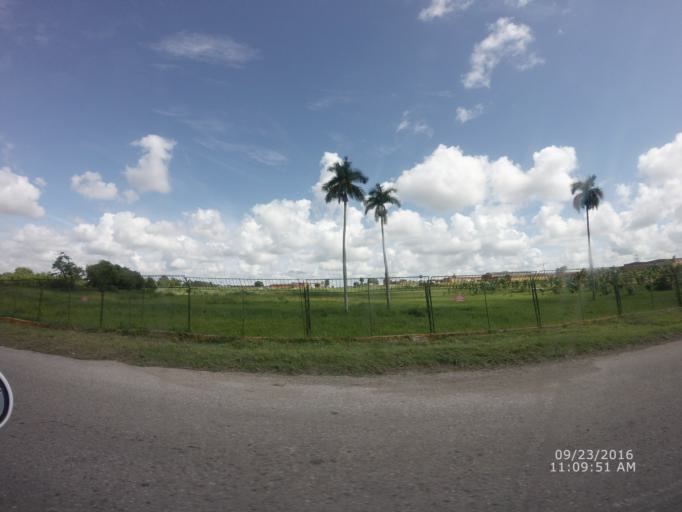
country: CU
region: La Habana
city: Arroyo Naranjo
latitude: 23.0191
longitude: -82.2509
